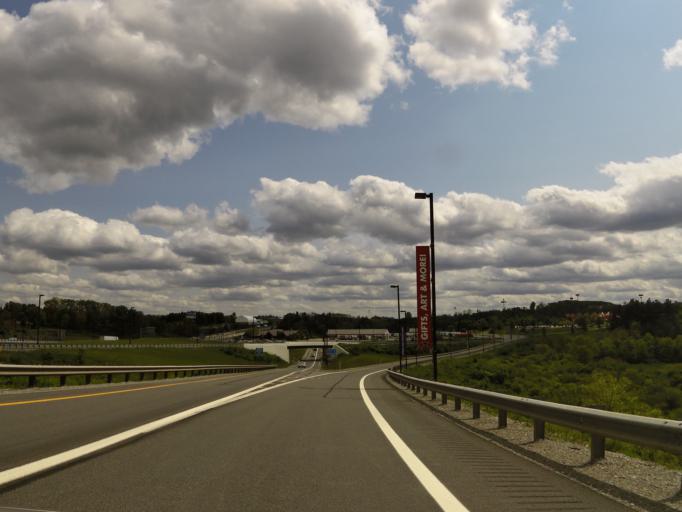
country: US
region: West Virginia
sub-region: Raleigh County
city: Prosperity
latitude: 37.8069
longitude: -81.2134
